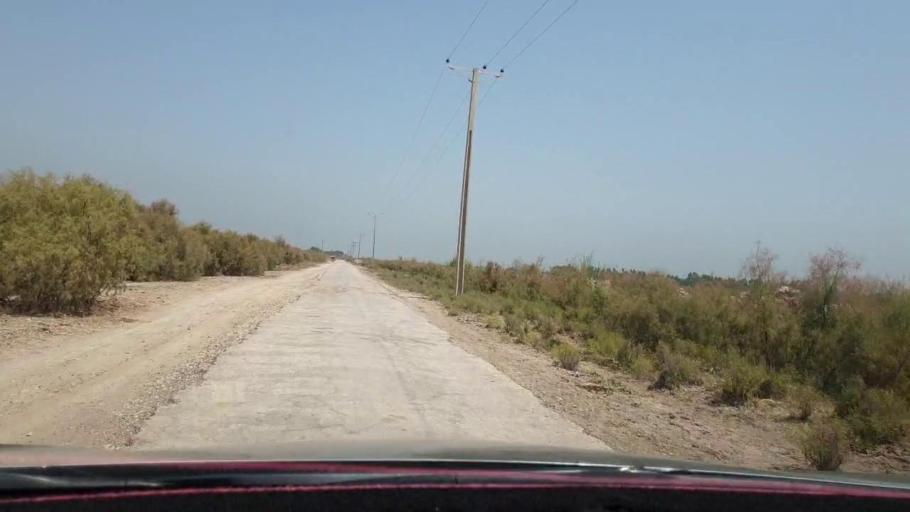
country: PK
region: Sindh
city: Warah
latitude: 27.4327
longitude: 67.7086
